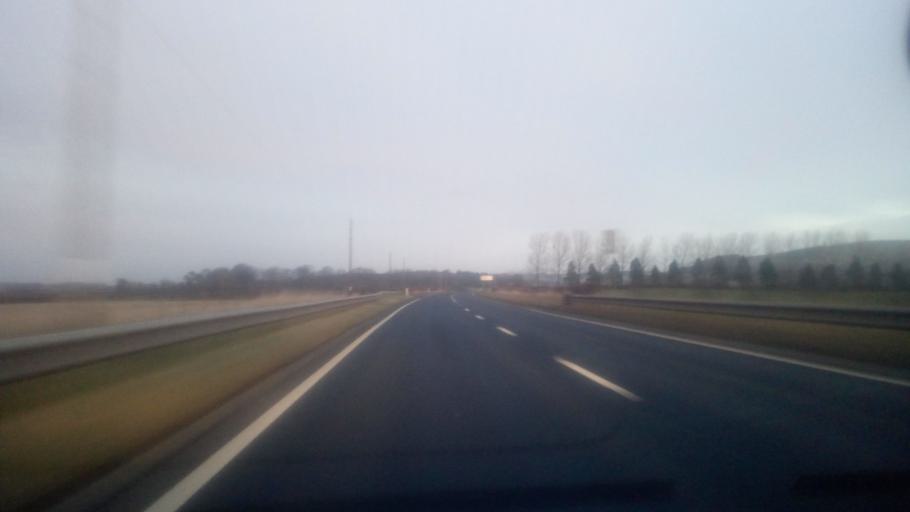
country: GB
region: Scotland
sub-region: The Scottish Borders
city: Lauder
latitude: 55.7550
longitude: -2.7766
